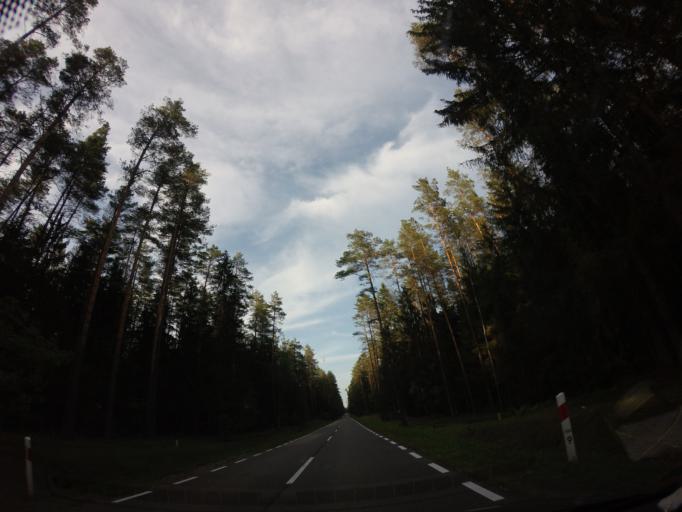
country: PL
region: Podlasie
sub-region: Powiat sejnenski
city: Krasnopol
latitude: 53.9675
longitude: 23.2459
